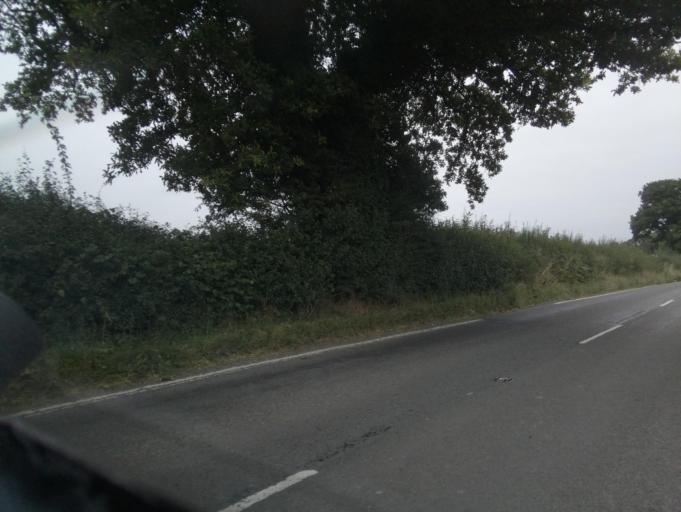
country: GB
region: England
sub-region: Derbyshire
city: Duffield
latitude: 53.0140
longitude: -1.5389
